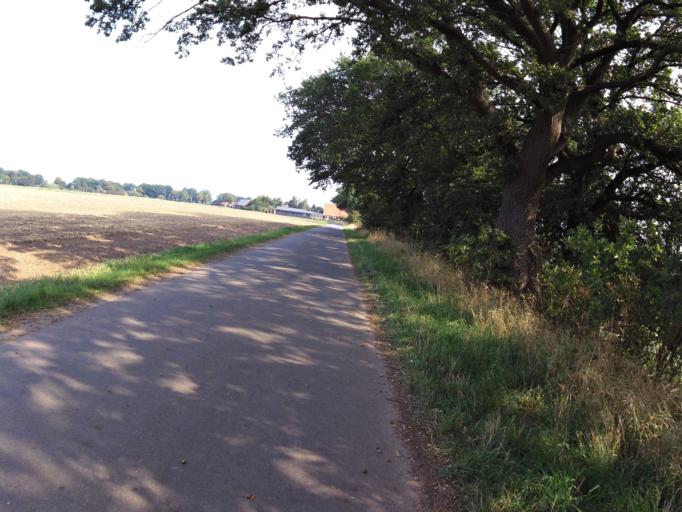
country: DE
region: Lower Saxony
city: Stolzenau
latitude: 52.4847
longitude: 9.0223
